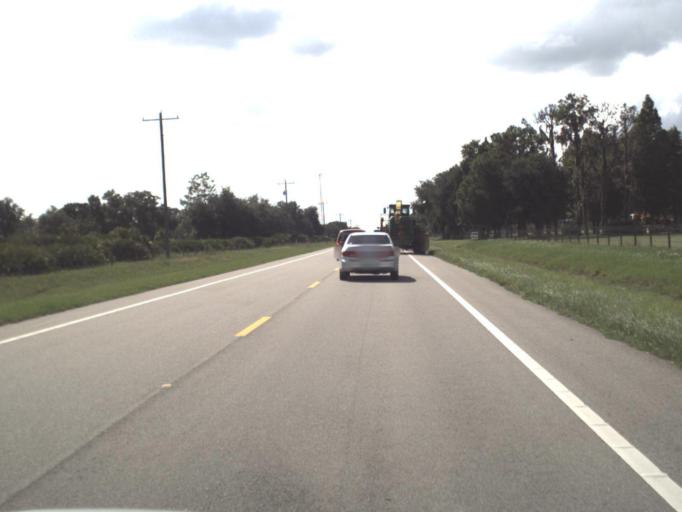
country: US
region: Florida
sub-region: Hillsborough County
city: Wimauma
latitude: 27.4738
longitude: -82.2357
